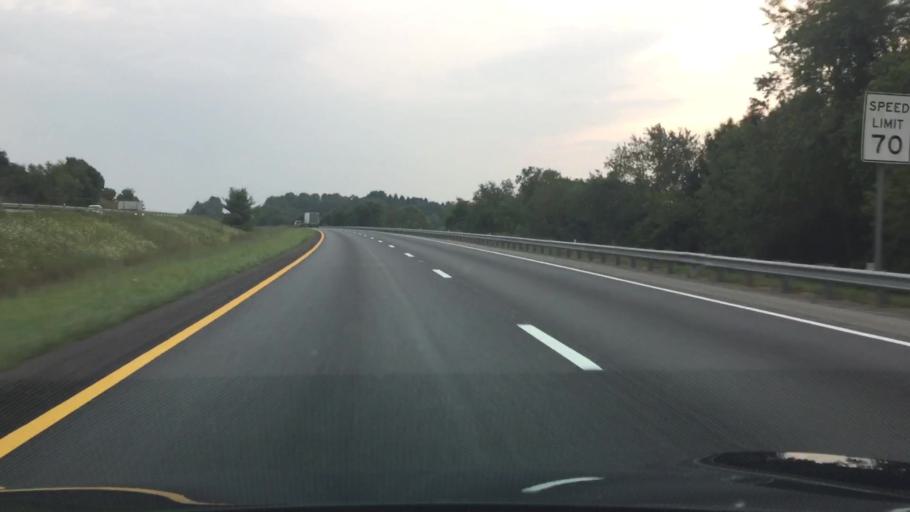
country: US
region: Virginia
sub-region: Montgomery County
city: Christiansburg
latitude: 37.1137
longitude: -80.4350
